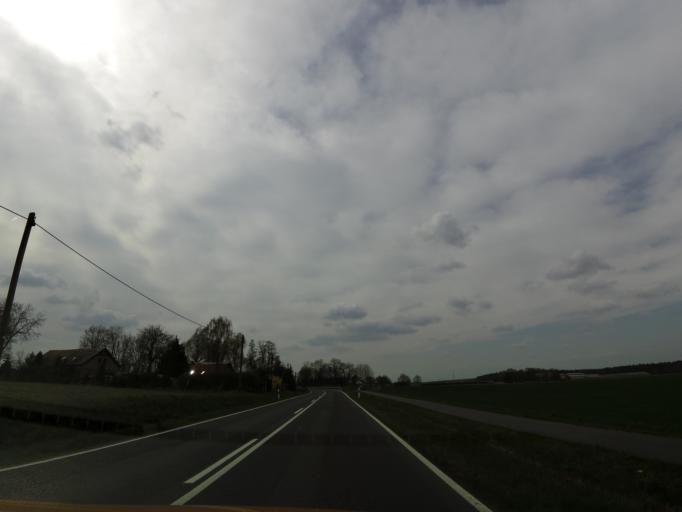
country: DE
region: Brandenburg
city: Jacobsdorf
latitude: 52.3579
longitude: 14.3326
